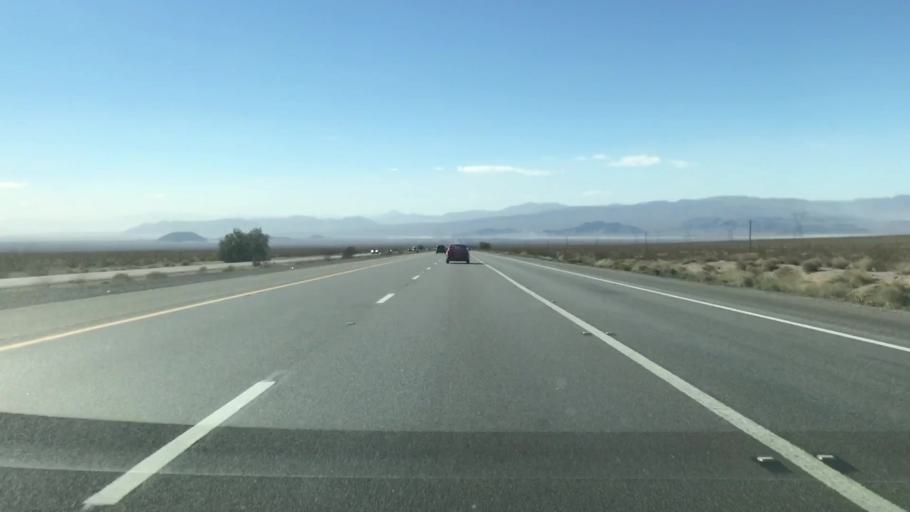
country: US
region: Nevada
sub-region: Clark County
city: Sandy Valley
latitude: 35.3435
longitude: -115.9518
